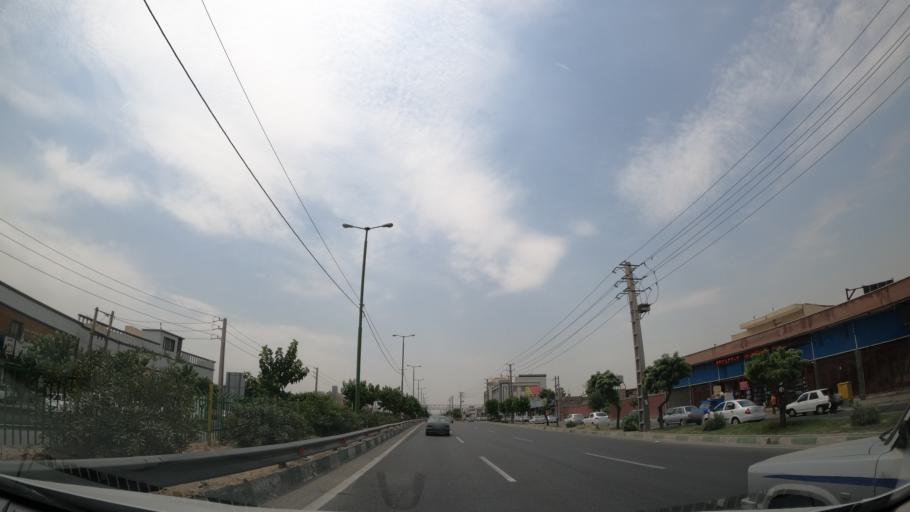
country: IR
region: Tehran
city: Tehran
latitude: 35.6762
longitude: 51.2952
